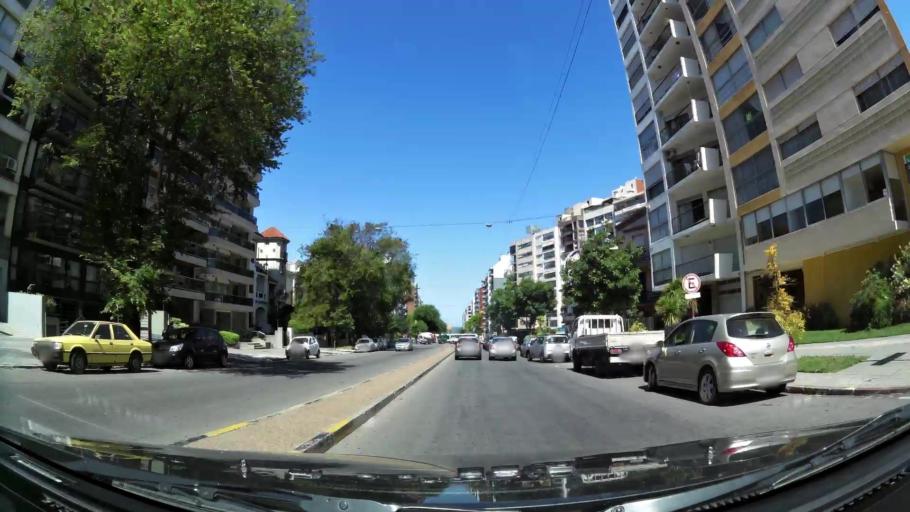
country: UY
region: Montevideo
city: Montevideo
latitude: -34.9137
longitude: -56.1549
